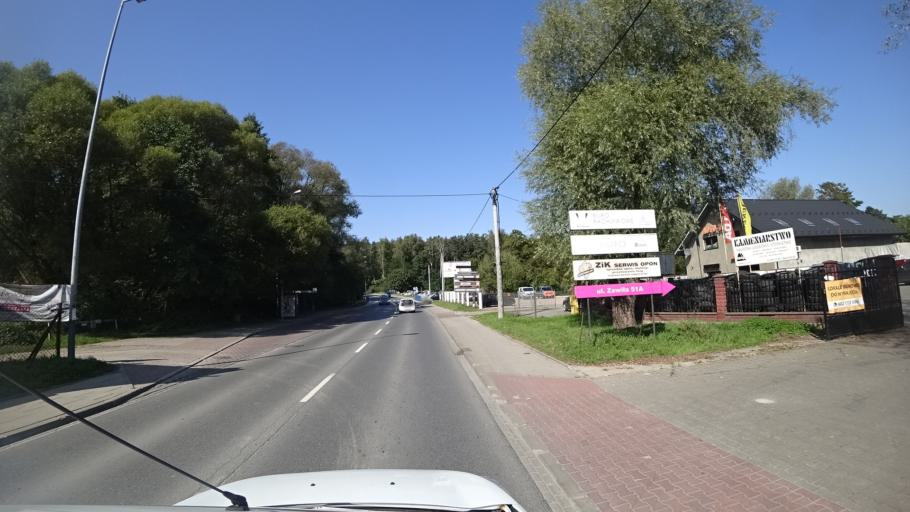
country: PL
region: Lesser Poland Voivodeship
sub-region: Powiat krakowski
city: Libertow
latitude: 50.0084
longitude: 19.9154
